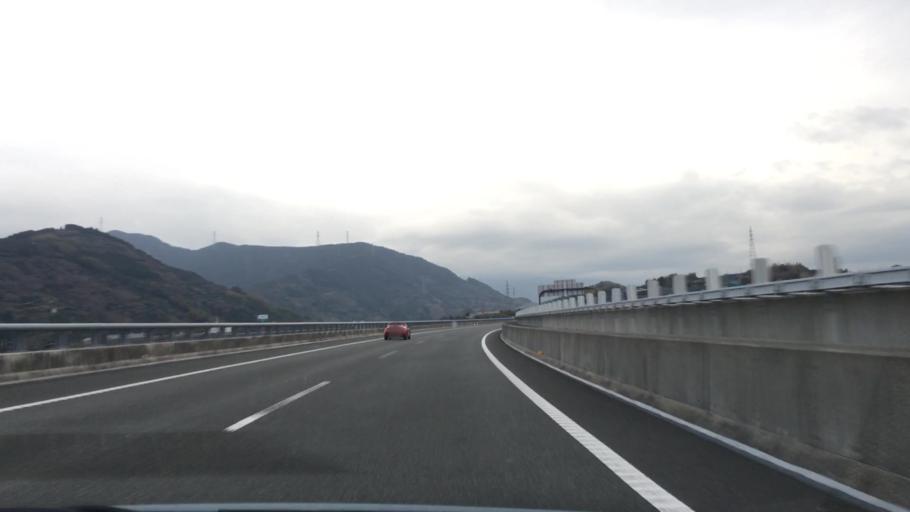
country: JP
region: Shizuoka
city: Shizuoka-shi
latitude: 35.0537
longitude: 138.4838
